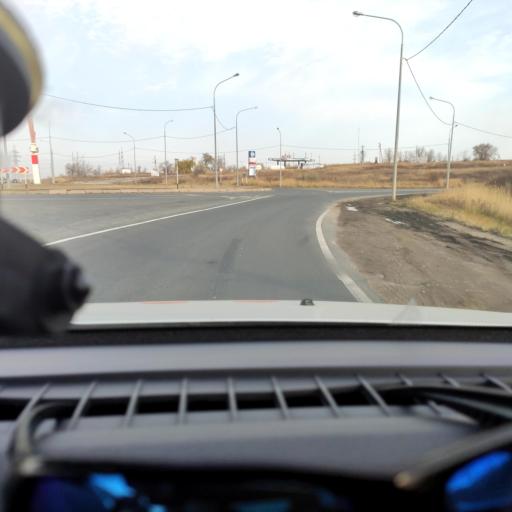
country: RU
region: Samara
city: Chapayevsk
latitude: 52.9965
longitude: 49.7683
